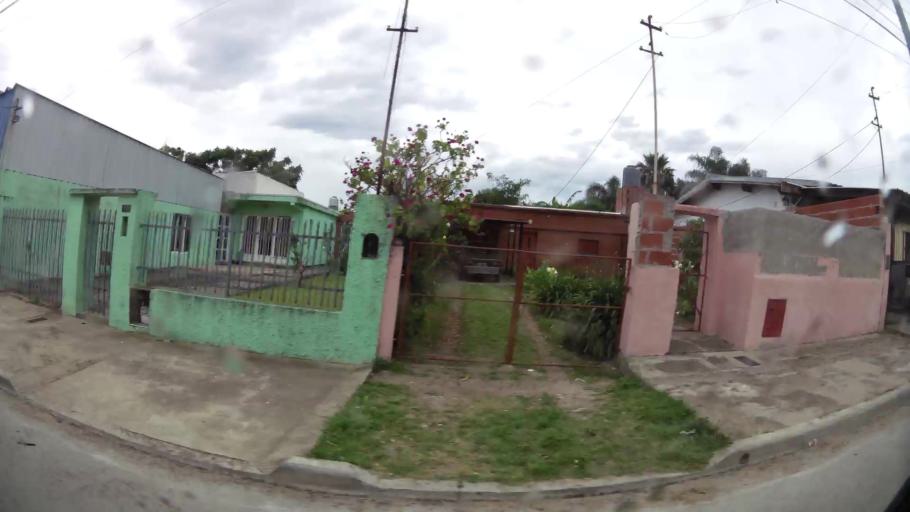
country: AR
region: Buenos Aires
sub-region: Partido de Zarate
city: Zarate
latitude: -34.0826
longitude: -59.0387
